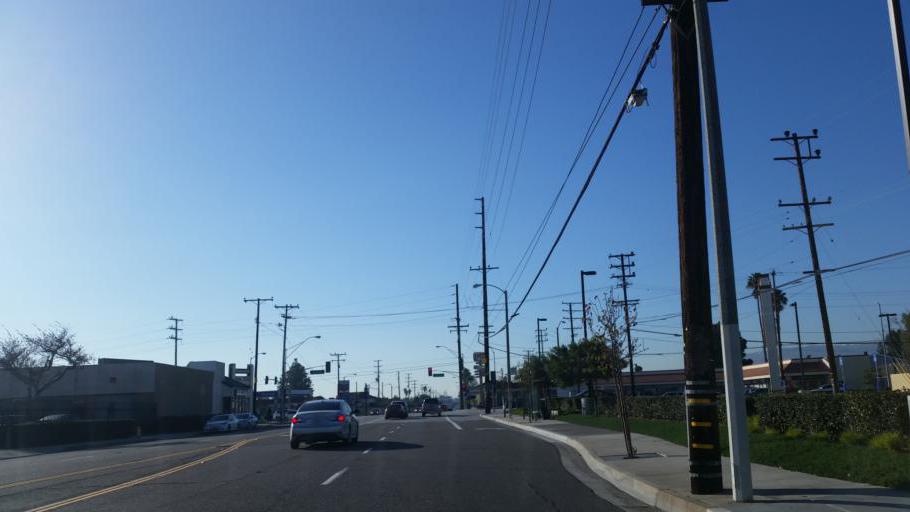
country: US
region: California
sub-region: Los Angeles County
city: West Carson
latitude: 33.8142
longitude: -118.2983
